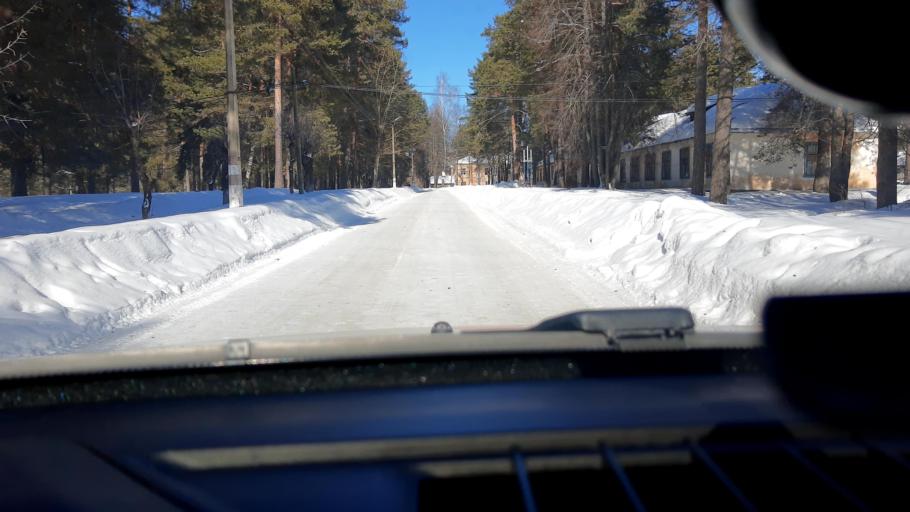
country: RU
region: Nizjnij Novgorod
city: Yuganets
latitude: 56.2466
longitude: 43.2321
